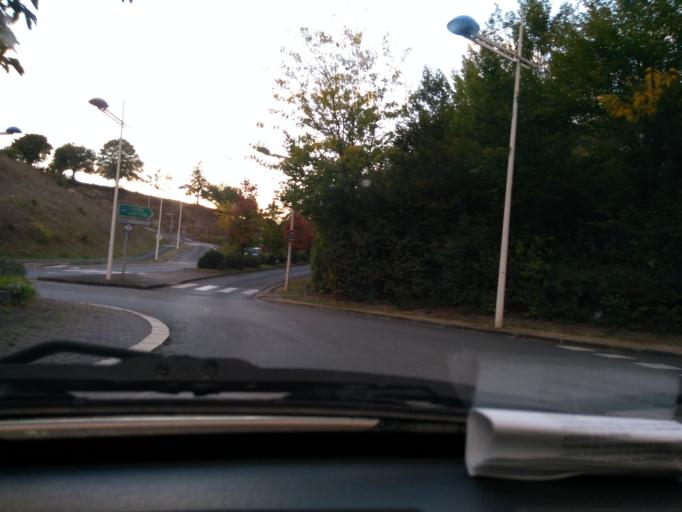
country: FR
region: Poitou-Charentes
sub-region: Departement de la Charente
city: Angouleme
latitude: 45.6416
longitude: 0.1451
